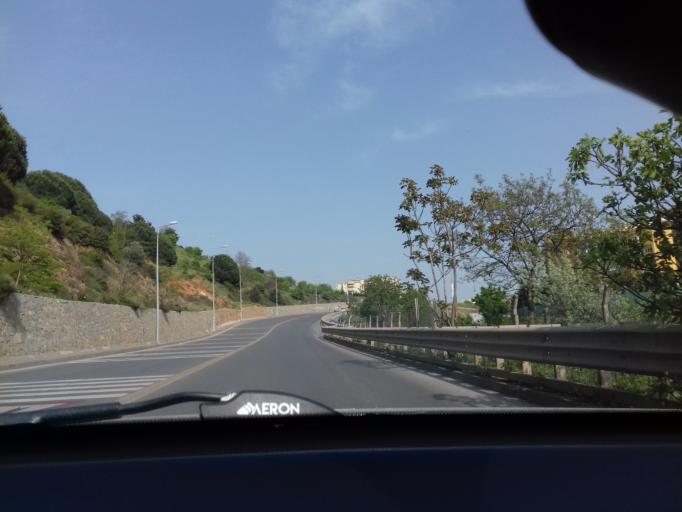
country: TR
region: Istanbul
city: Pendik
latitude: 40.9080
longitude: 29.2388
